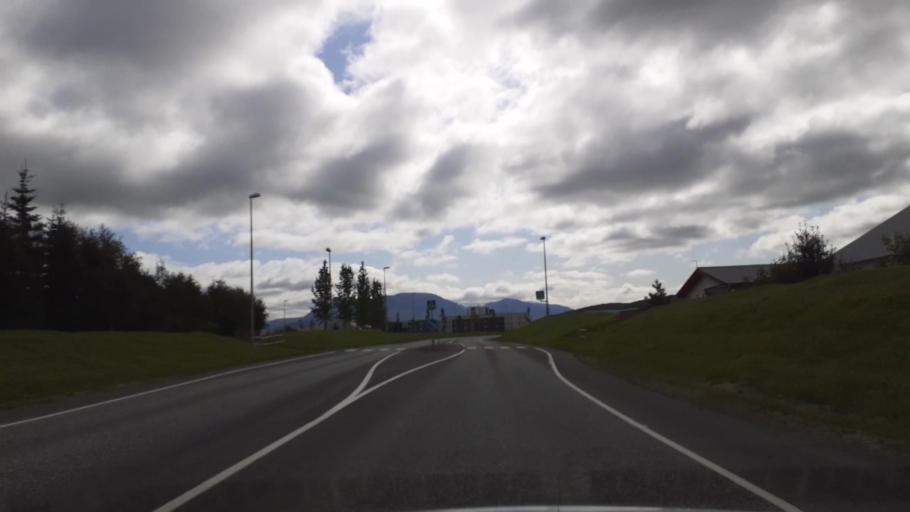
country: IS
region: Northeast
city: Akureyri
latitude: 65.6720
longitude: -18.1081
